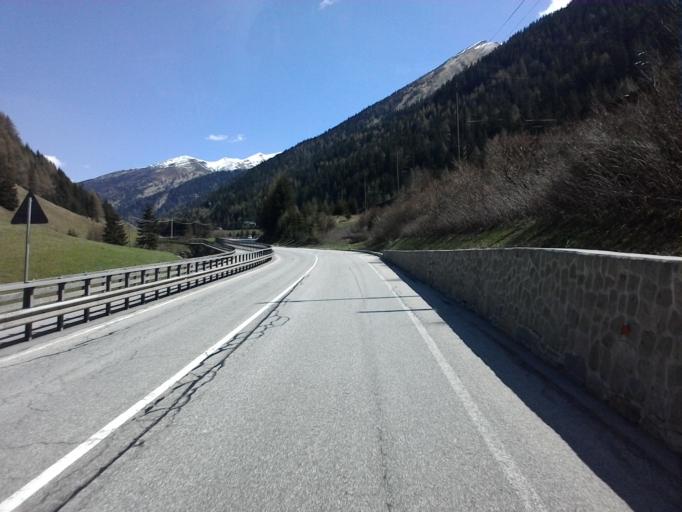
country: IT
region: Trentino-Alto Adige
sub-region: Bolzano
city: Ried
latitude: 46.9817
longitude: 11.4908
